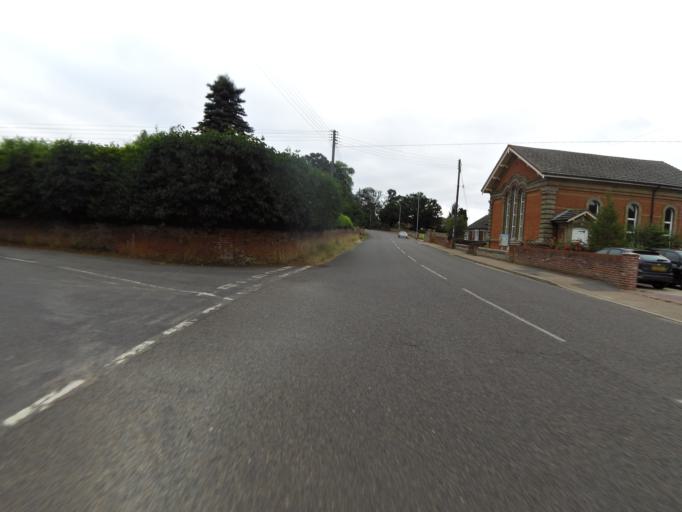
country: GB
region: England
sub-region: Suffolk
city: Bramford
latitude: 52.0777
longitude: 1.0955
